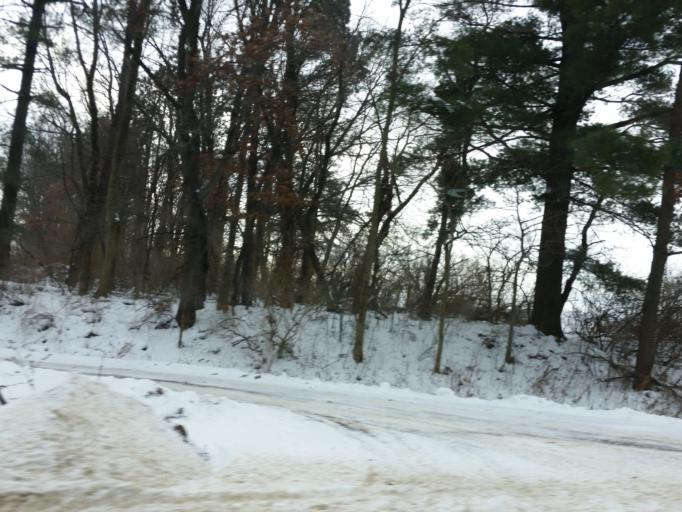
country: US
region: Iowa
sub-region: Dubuque County
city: Peosta
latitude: 42.3839
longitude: -90.7957
